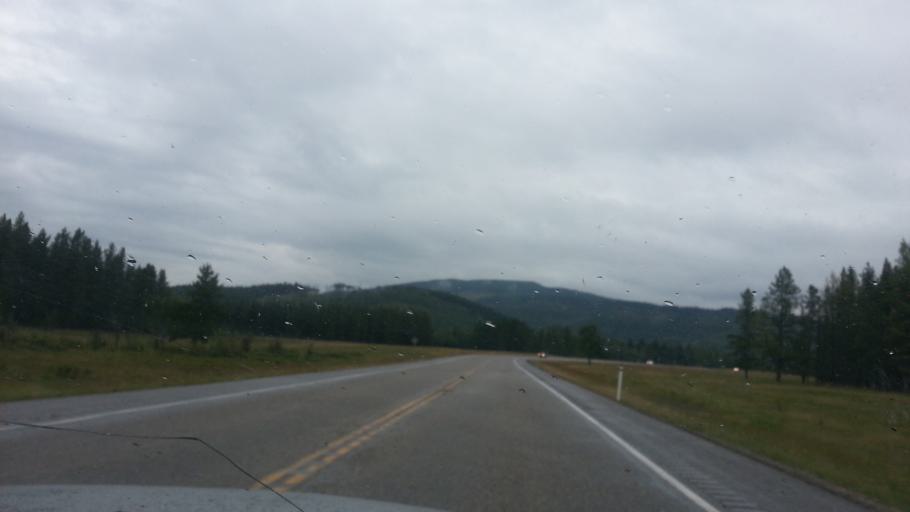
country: CA
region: Alberta
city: Cochrane
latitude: 50.8922
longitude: -114.7037
